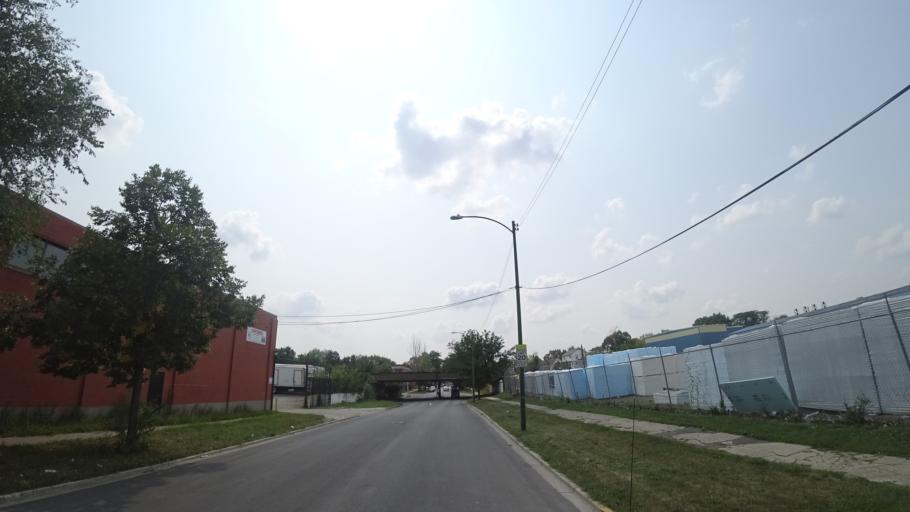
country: US
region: Illinois
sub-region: Cook County
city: Cicero
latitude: 41.8485
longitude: -87.7295
